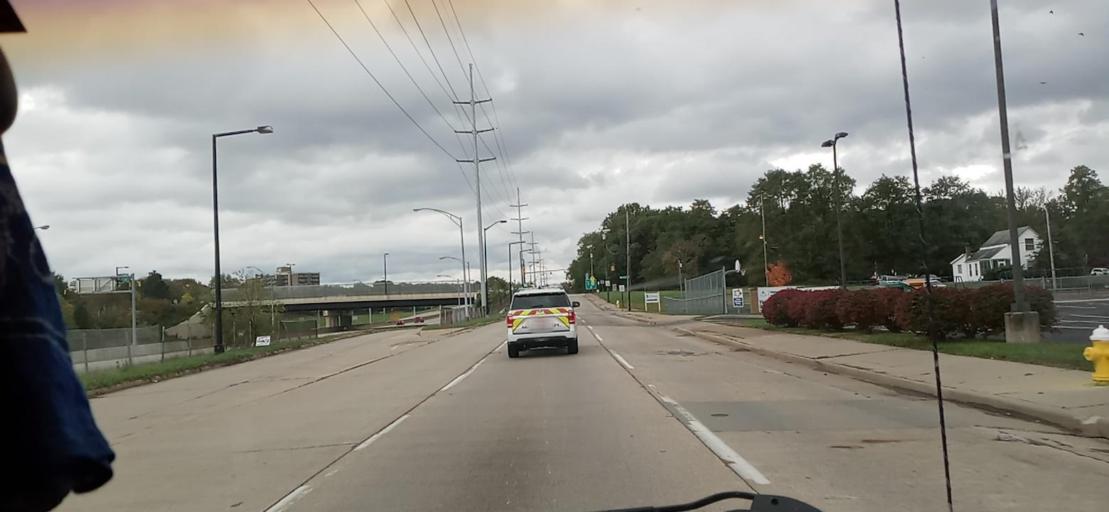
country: US
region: Ohio
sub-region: Summit County
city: Akron
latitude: 41.0723
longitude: -81.5384
